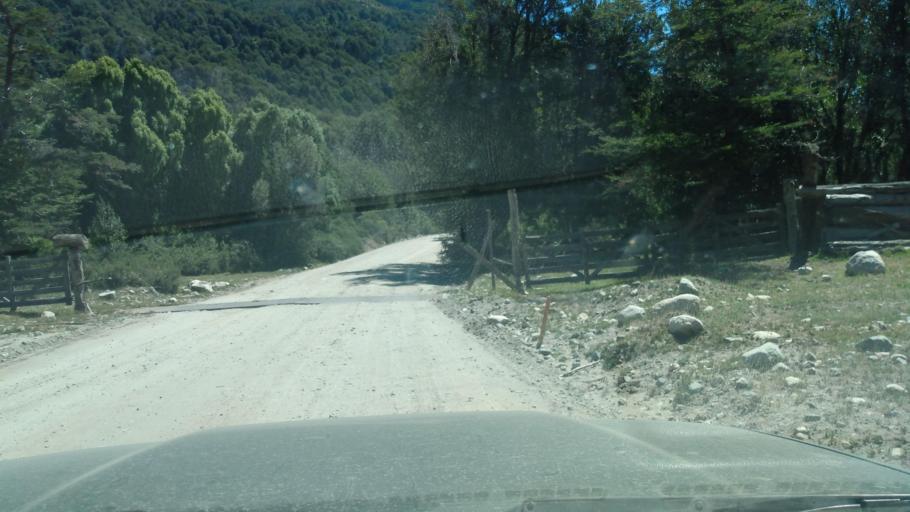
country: AR
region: Neuquen
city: Villa La Angostura
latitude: -40.6228
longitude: -71.5166
